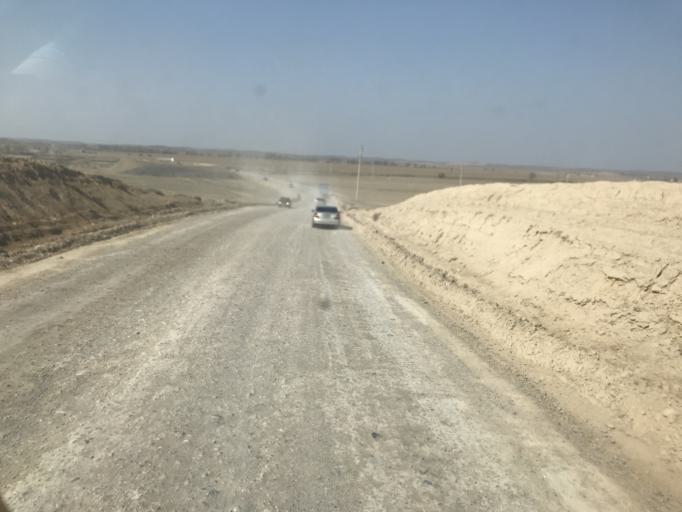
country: KG
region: Chuy
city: Bystrovka
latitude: 43.3222
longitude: 76.0426
